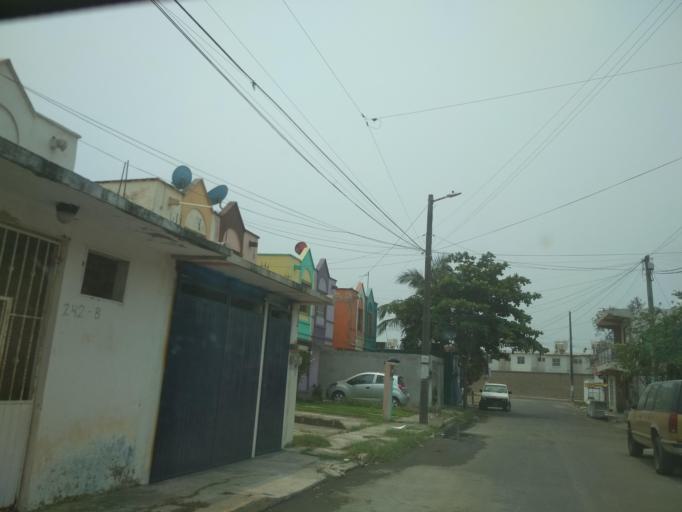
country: MX
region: Veracruz
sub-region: Veracruz
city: Rio Medio [Granja]
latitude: 19.2111
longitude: -96.2038
